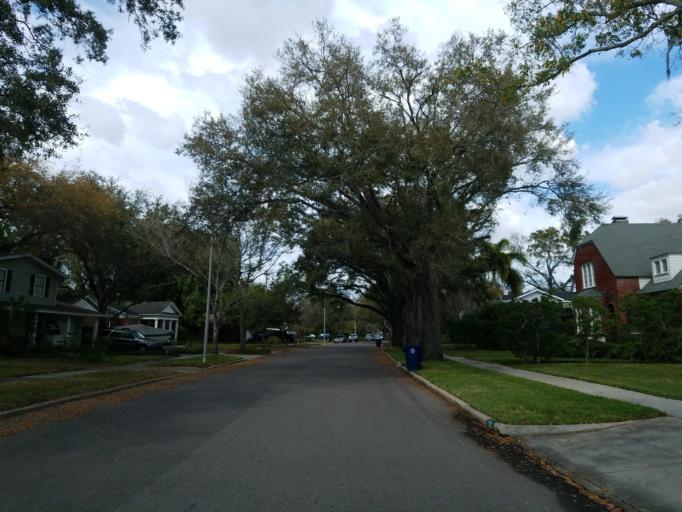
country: US
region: Florida
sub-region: Hillsborough County
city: Tampa
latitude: 27.9262
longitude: -82.4572
